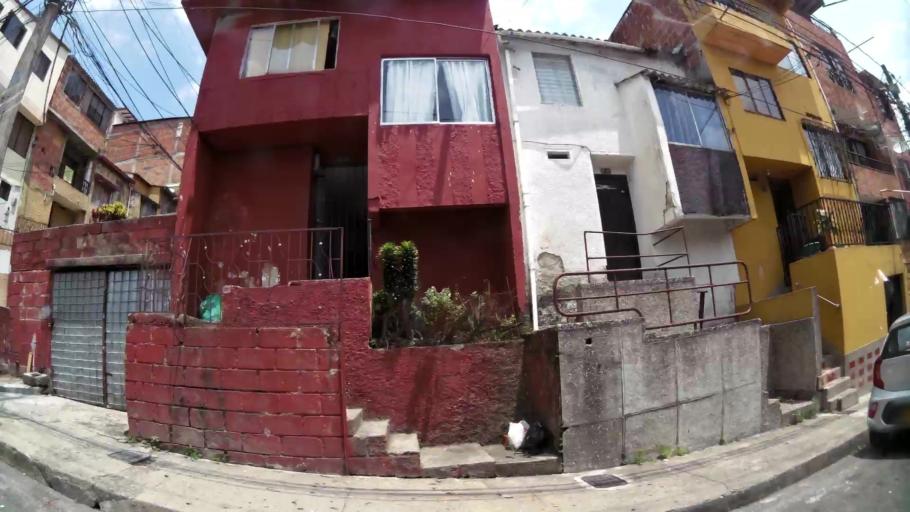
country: CO
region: Antioquia
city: Itagui
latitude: 6.1806
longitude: -75.6042
